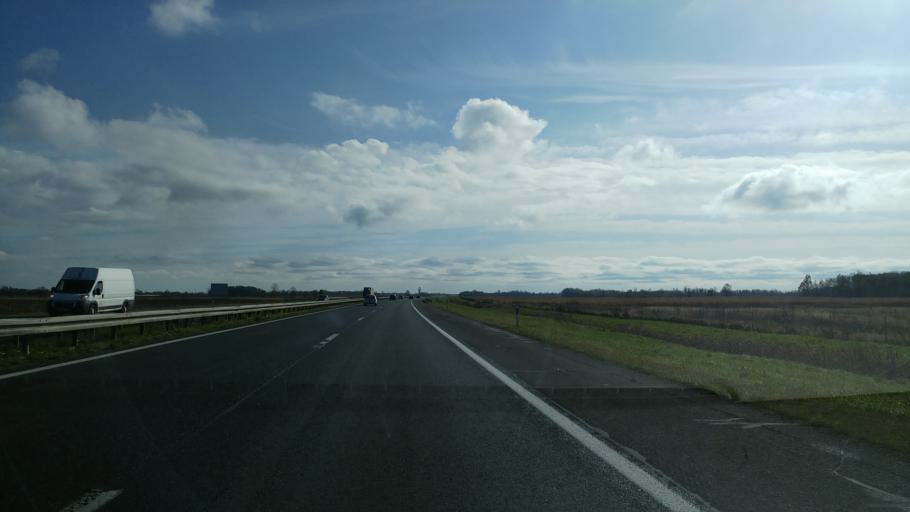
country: HR
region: Zagrebacka
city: Lupoglav
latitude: 45.7349
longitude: 16.3342
